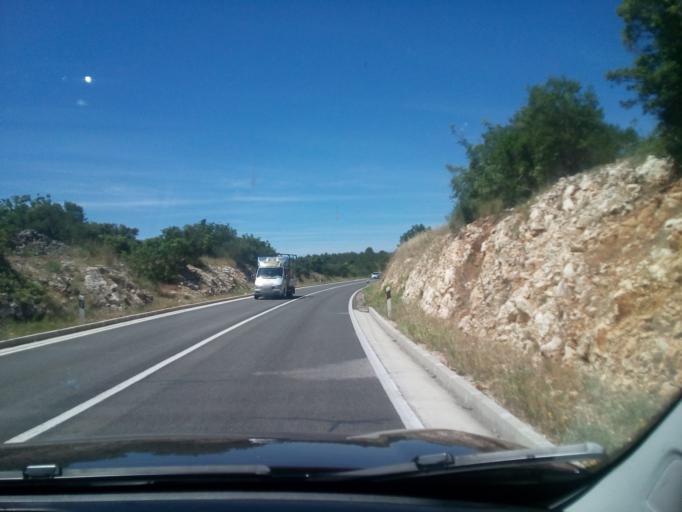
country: HR
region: Sibensko-Kniniska
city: Zaton
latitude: 43.7580
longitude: 15.8292
